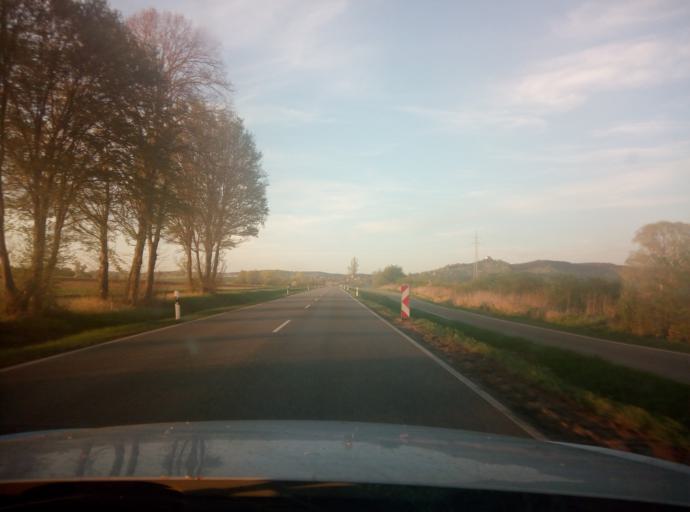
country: DE
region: Baden-Wuerttemberg
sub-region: Tuebingen Region
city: Rottenburg
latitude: 48.4936
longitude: 8.9566
